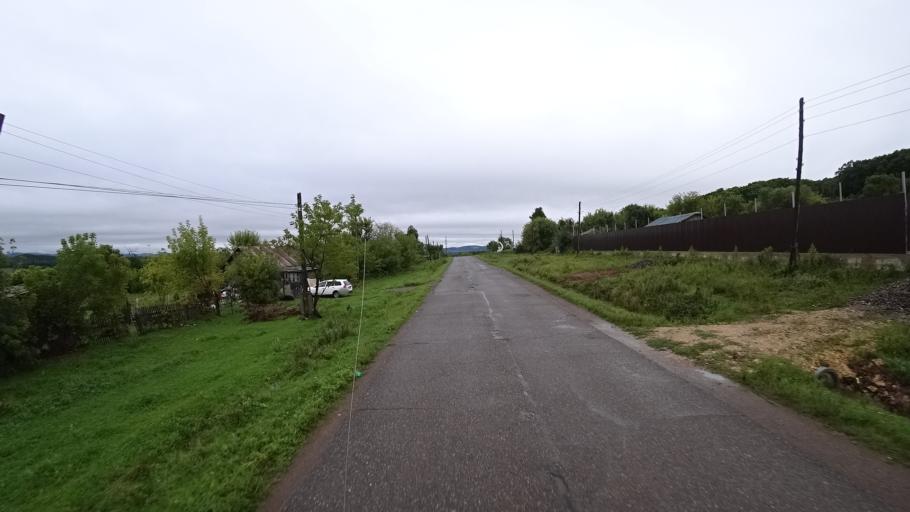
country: RU
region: Primorskiy
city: Monastyrishche
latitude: 44.2656
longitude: 132.4205
